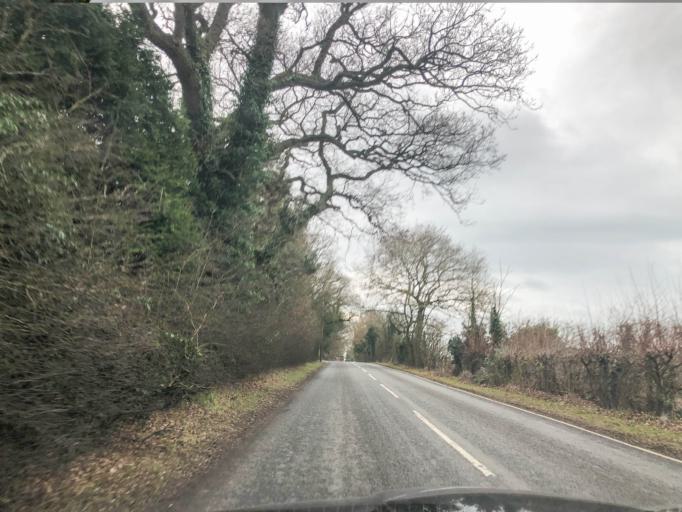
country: GB
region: England
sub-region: Warwickshire
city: Wroxall
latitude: 52.3243
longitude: -1.6691
